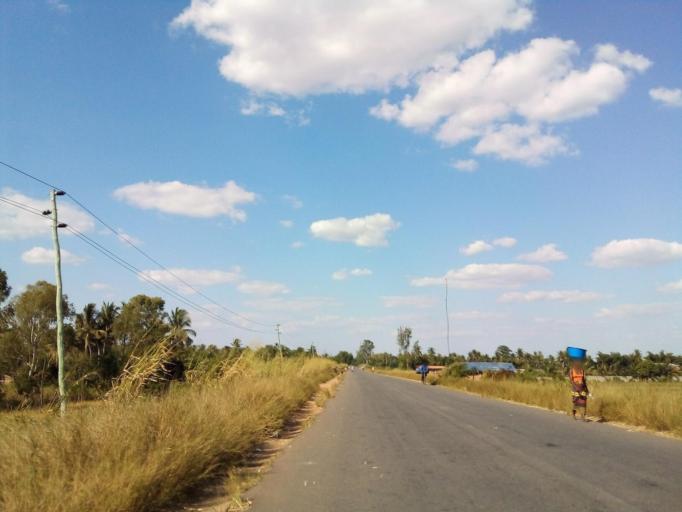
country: MZ
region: Zambezia
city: Quelimane
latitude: -17.5781
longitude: 36.6963
